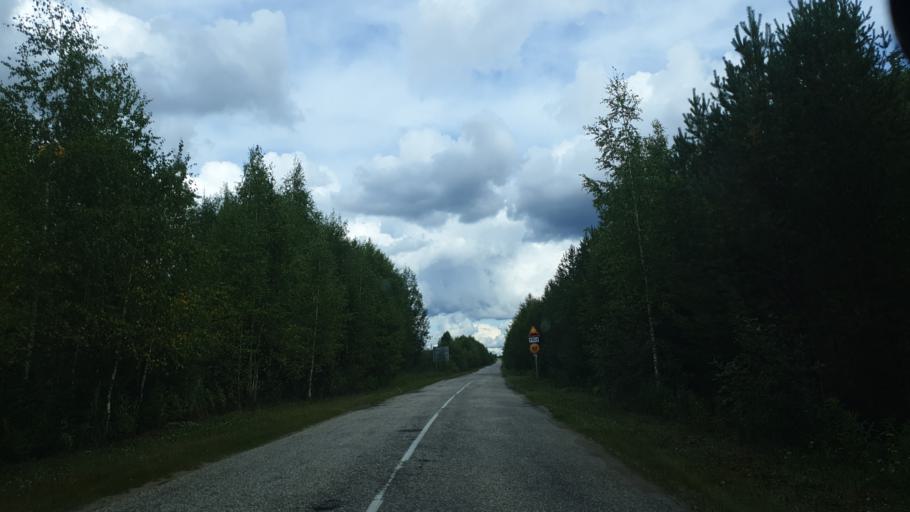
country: RU
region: Komi Republic
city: Aykino
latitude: 61.9362
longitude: 50.1565
